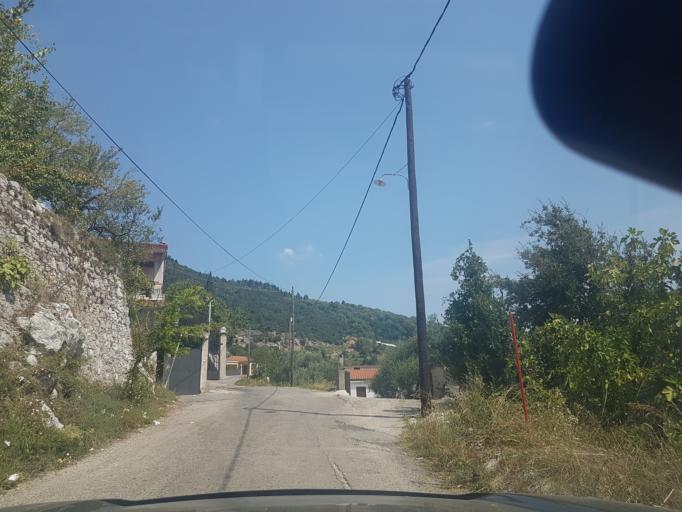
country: GR
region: Central Greece
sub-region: Nomos Evvoias
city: Yimnon
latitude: 38.6197
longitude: 23.8880
